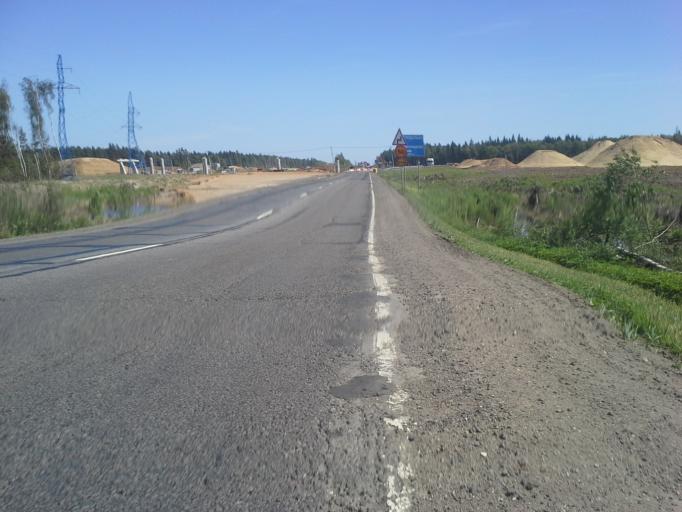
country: RU
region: Moskovskaya
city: Aprelevka
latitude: 55.4543
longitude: 37.1153
